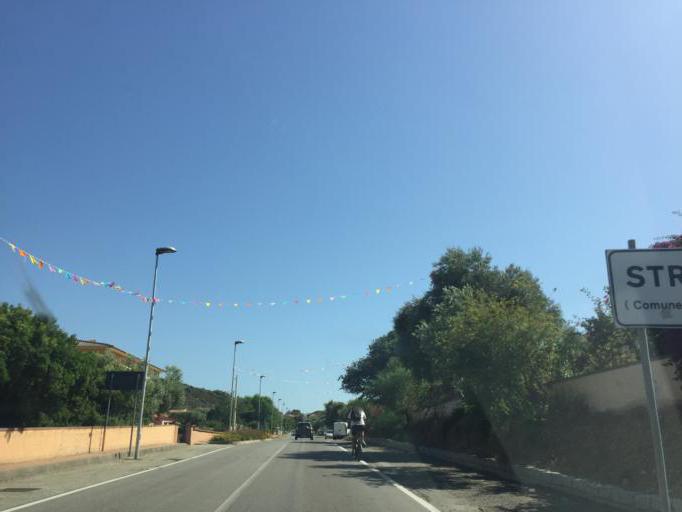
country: IT
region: Sardinia
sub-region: Provincia di Olbia-Tempio
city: San Teodoro
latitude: 40.7487
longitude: 9.6470
